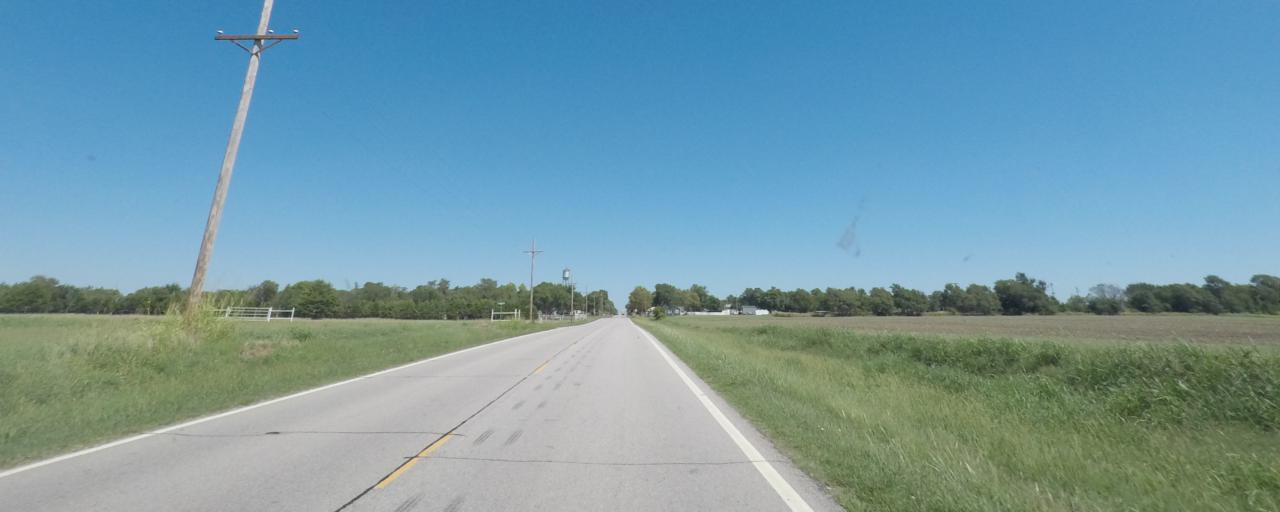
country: US
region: Kansas
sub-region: Sumner County
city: Caldwell
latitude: 37.0428
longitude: -97.4011
